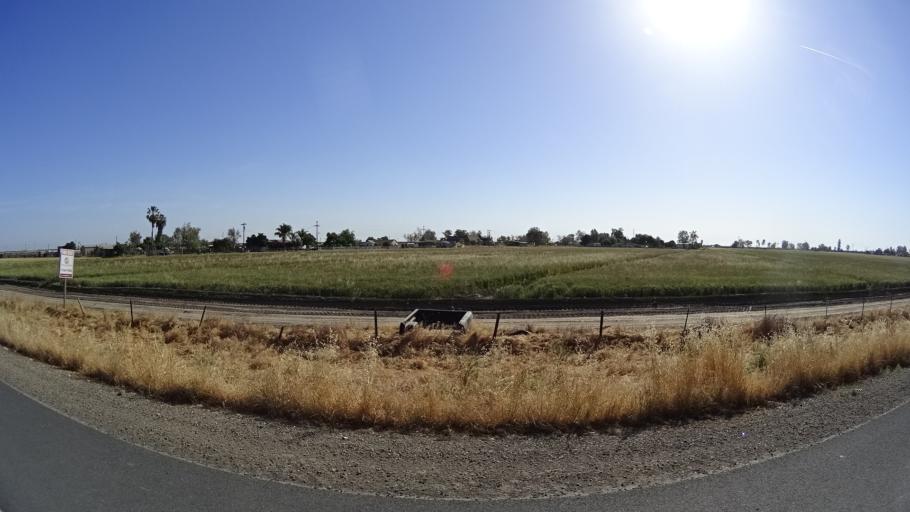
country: US
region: California
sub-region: Kings County
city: Corcoran
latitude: 36.1188
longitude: -119.5713
